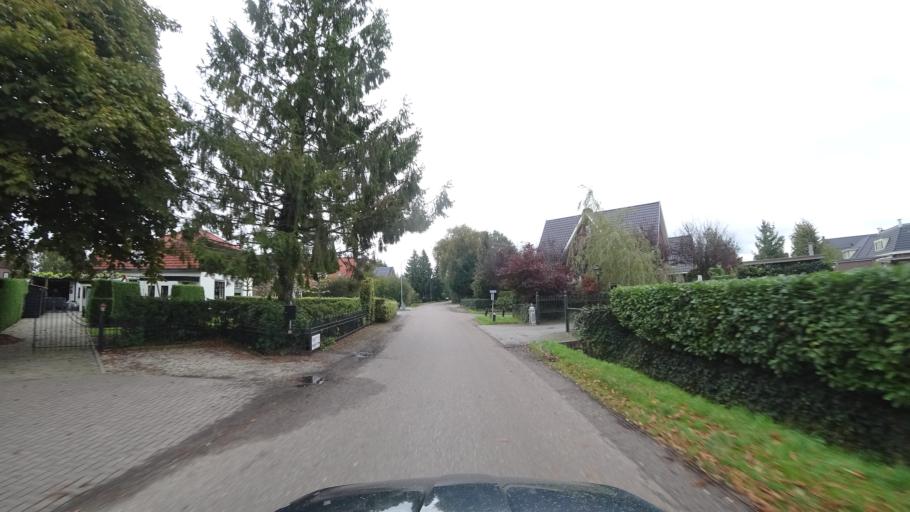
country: NL
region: Gelderland
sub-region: Gemeente Nijkerk
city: Nijkerk
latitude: 52.1997
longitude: 5.4507
